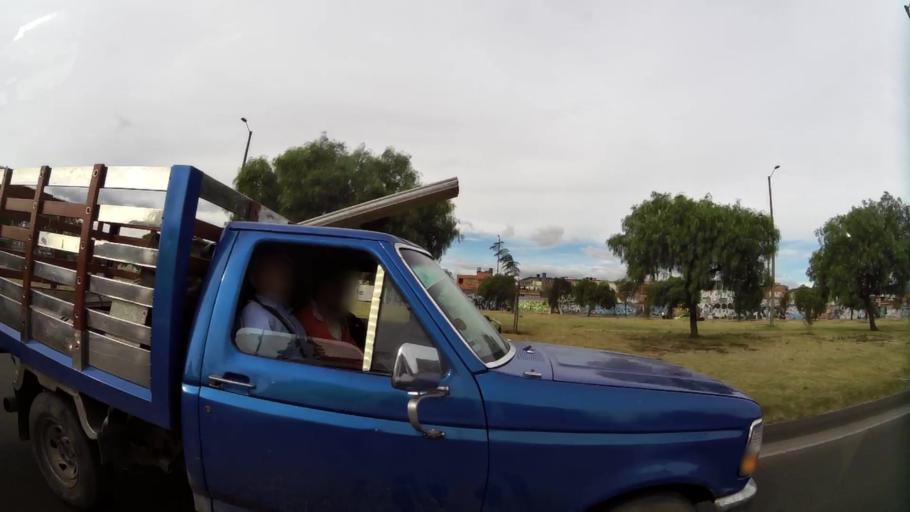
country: CO
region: Bogota D.C.
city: Bogota
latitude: 4.6331
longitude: -74.1513
